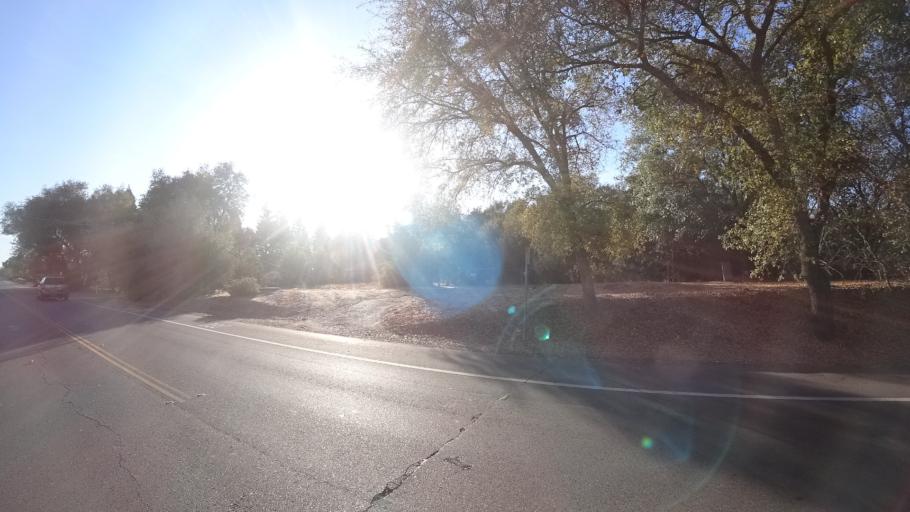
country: US
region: California
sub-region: Sacramento County
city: Antelope
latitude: 38.6942
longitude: -121.3087
